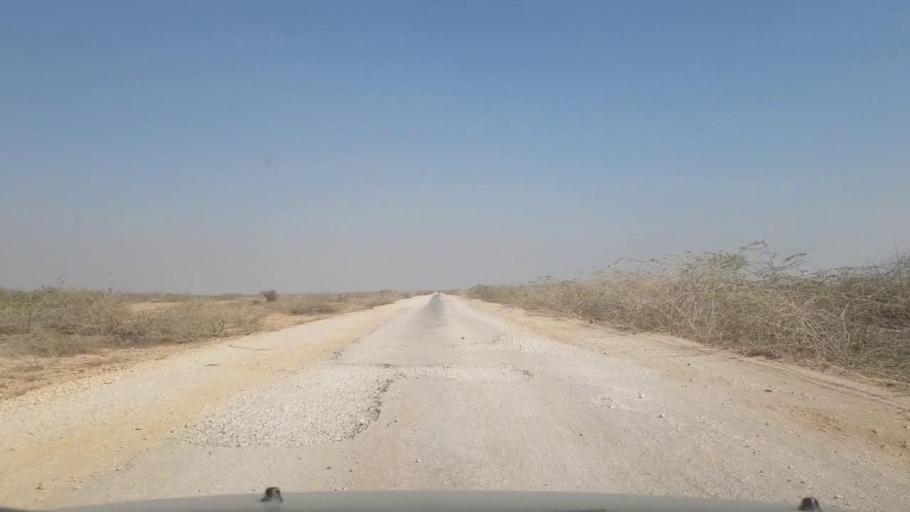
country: PK
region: Sindh
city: Thatta
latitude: 24.9031
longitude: 67.9229
